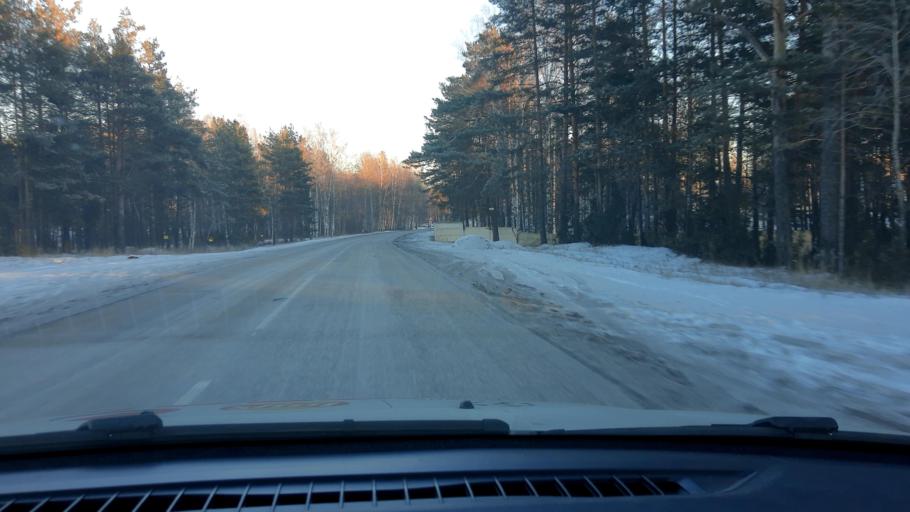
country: RU
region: Nizjnij Novgorod
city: Novosmolinskiy
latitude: 56.3202
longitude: 43.0127
